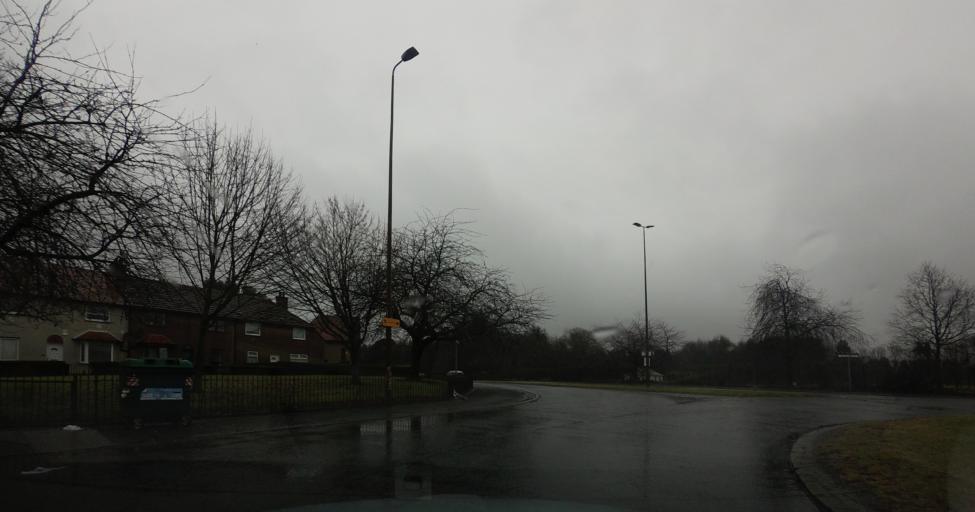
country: GB
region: Scotland
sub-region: Dundee City
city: Dundee
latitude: 56.4873
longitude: -2.9741
